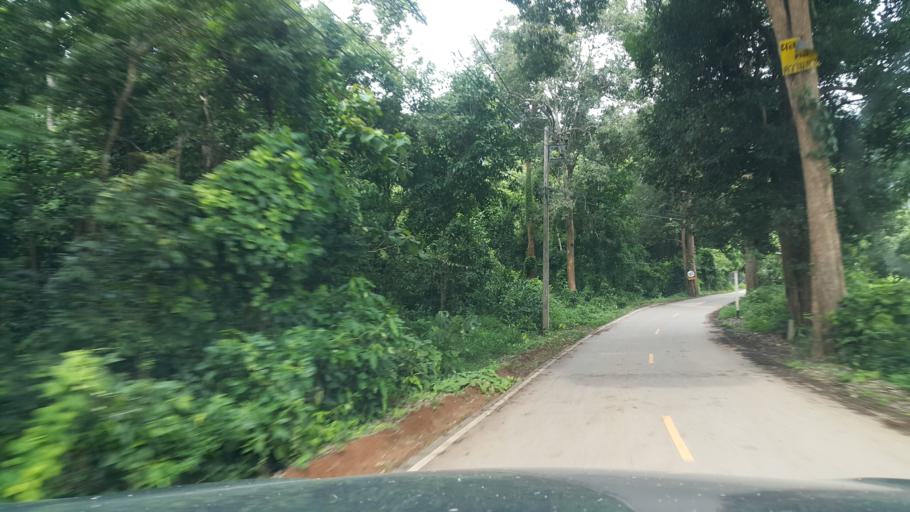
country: TH
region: Chiang Mai
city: San Sai
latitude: 18.9929
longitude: 99.1263
